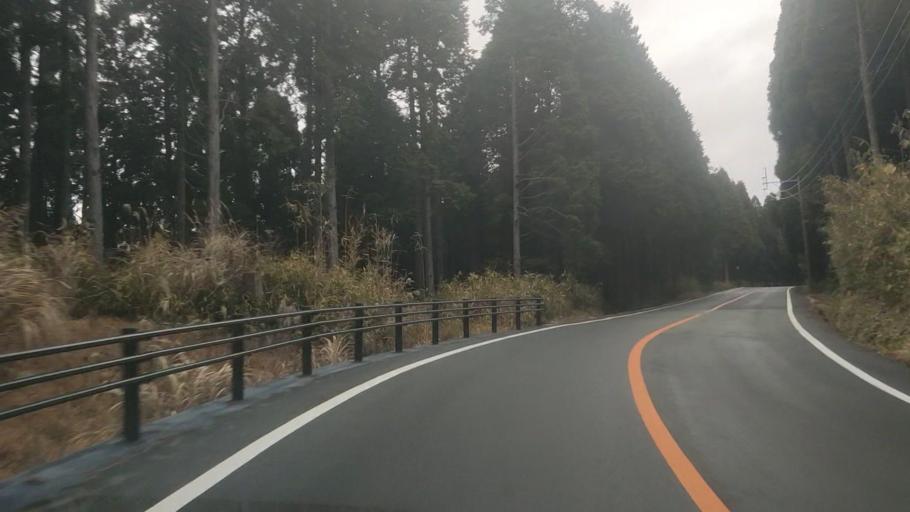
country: JP
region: Kumamoto
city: Aso
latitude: 32.8986
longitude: 131.0284
